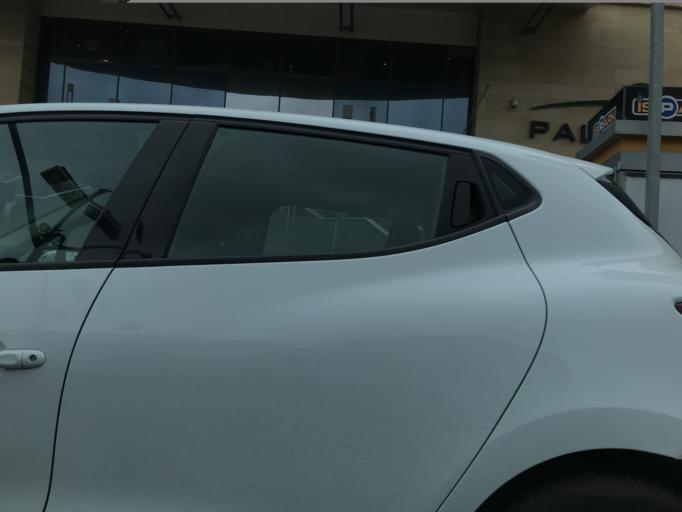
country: TR
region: Istanbul
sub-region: Atasehir
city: Atasehir
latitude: 40.9857
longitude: 29.0992
